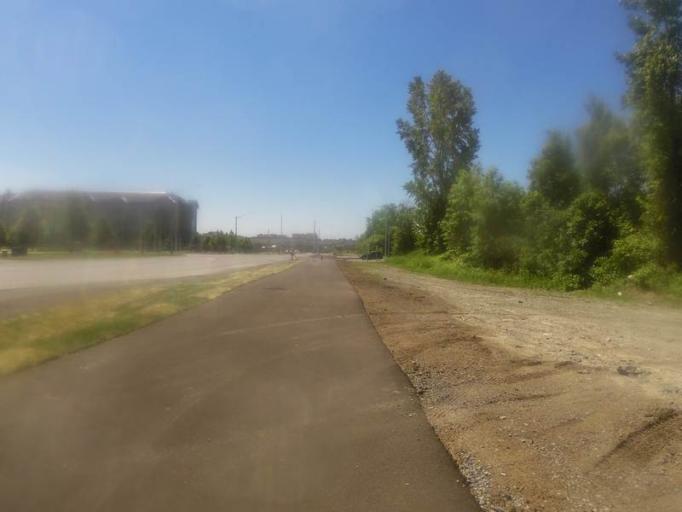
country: CA
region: Ontario
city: Kingston
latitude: 44.2702
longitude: -76.5592
